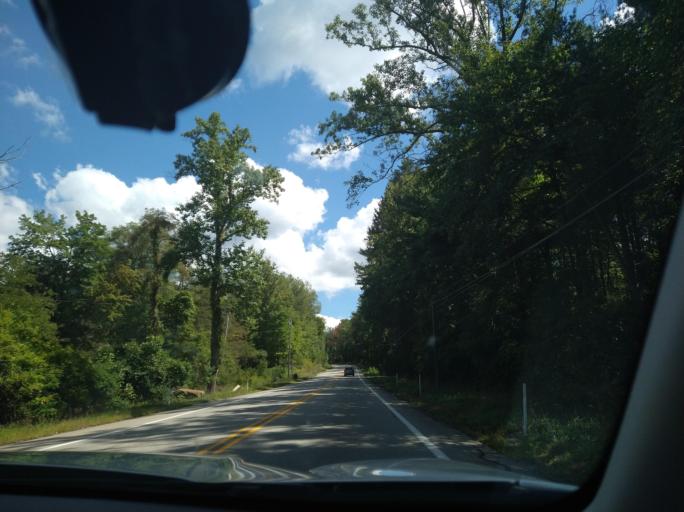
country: US
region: Pennsylvania
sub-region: Fayette County
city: Bear Rocks
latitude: 40.0803
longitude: -79.3262
